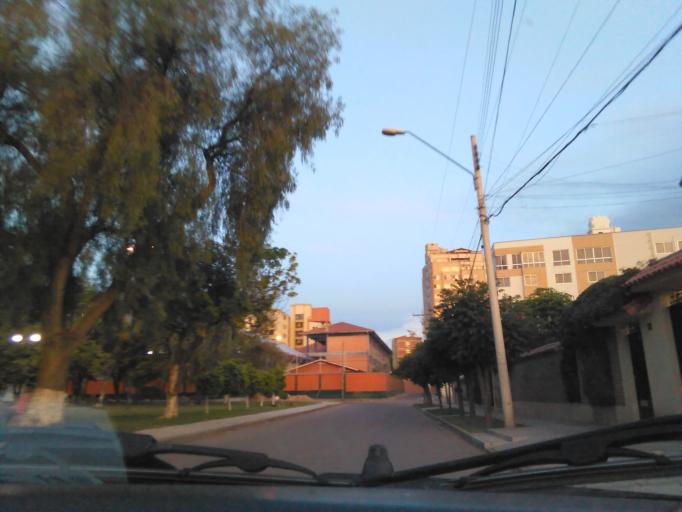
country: BO
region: Cochabamba
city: Cochabamba
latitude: -17.3707
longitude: -66.1656
